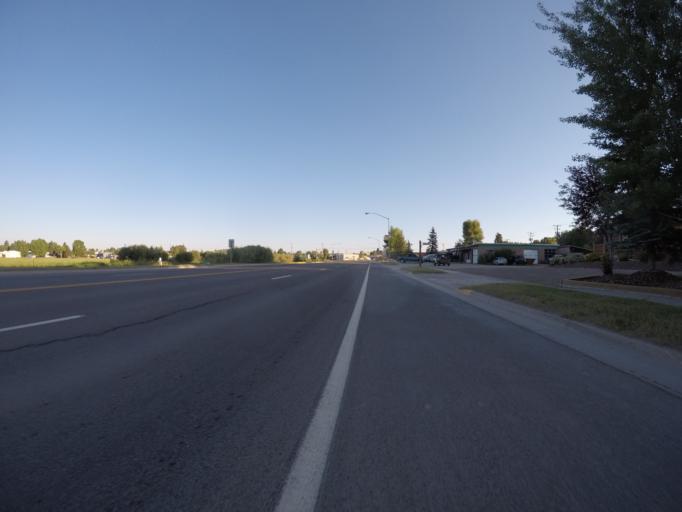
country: US
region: Wyoming
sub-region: Sublette County
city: Pinedale
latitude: 42.8642
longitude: -109.8537
